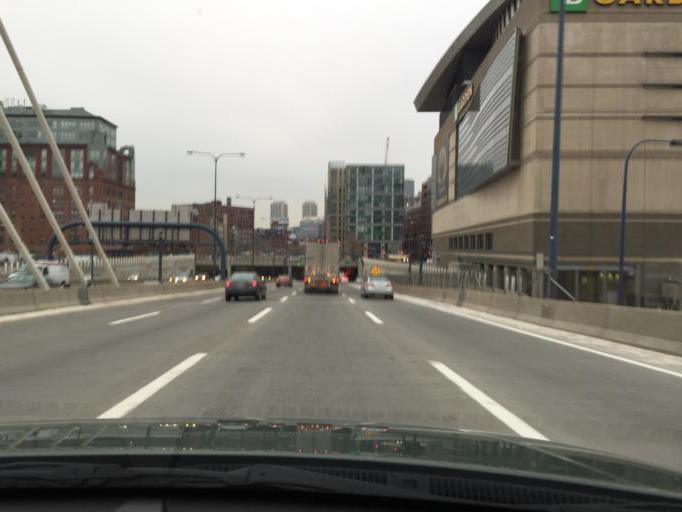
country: US
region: Massachusetts
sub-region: Suffolk County
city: Boston
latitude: 42.3677
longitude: -71.0622
